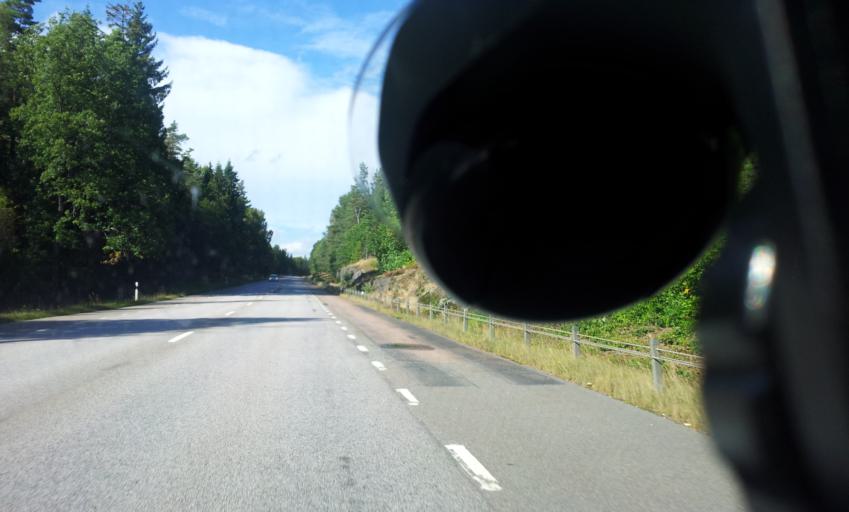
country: SE
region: Kalmar
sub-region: Vasterviks Kommun
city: Ankarsrum
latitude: 57.6197
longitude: 16.4668
